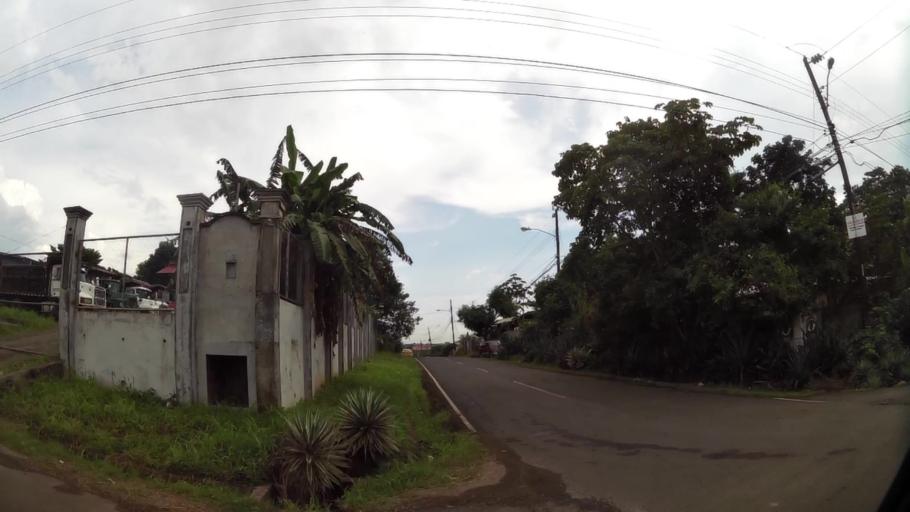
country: PA
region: Panama
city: Tocumen
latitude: 9.1109
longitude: -79.3764
